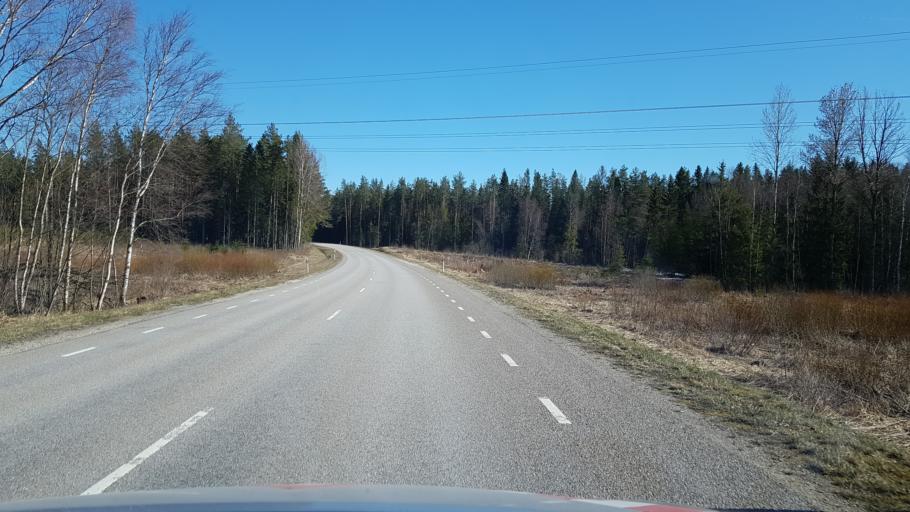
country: EE
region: Laeaene-Virumaa
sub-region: Viru-Nigula vald
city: Kunda
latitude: 59.3694
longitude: 26.5966
